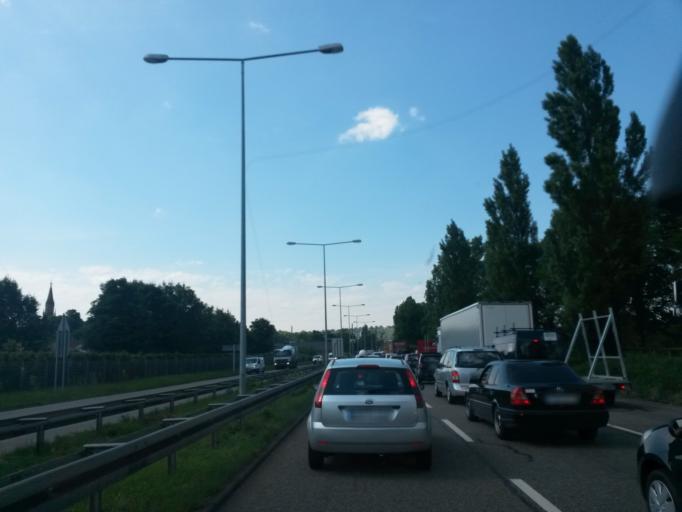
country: DE
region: Baden-Wuerttemberg
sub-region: Regierungsbezirk Stuttgart
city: Stuttgart-Ost
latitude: 48.7950
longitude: 9.2154
